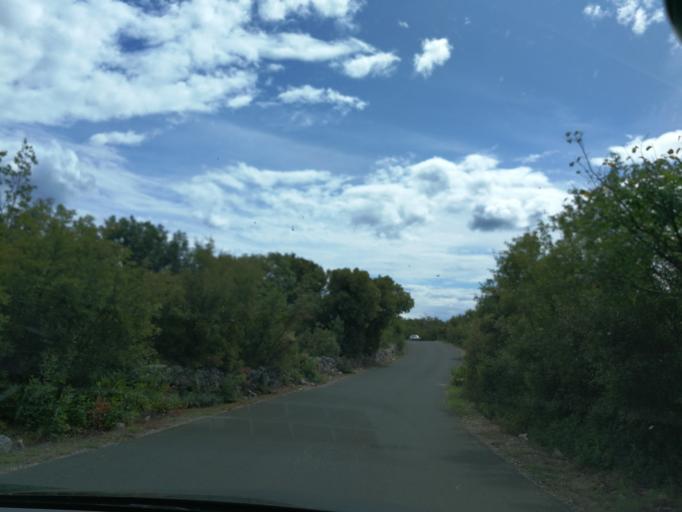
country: HR
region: Primorsko-Goranska
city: Omisalj
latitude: 45.2006
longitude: 14.5727
